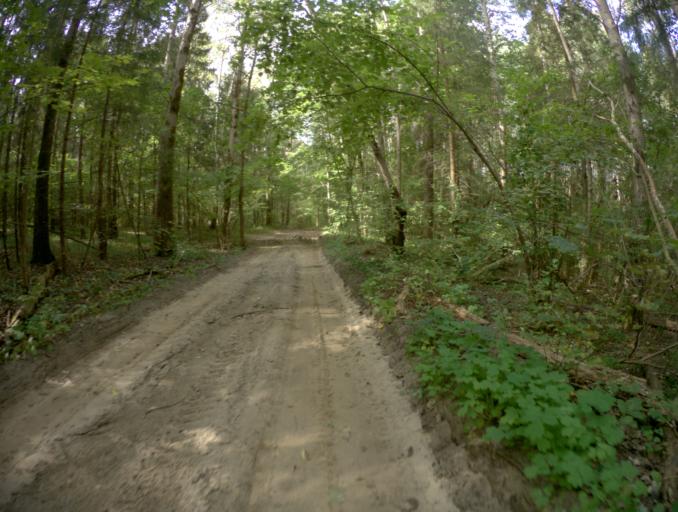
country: RU
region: Vladimir
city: Raduzhnyy
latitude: 56.0220
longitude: 40.2787
